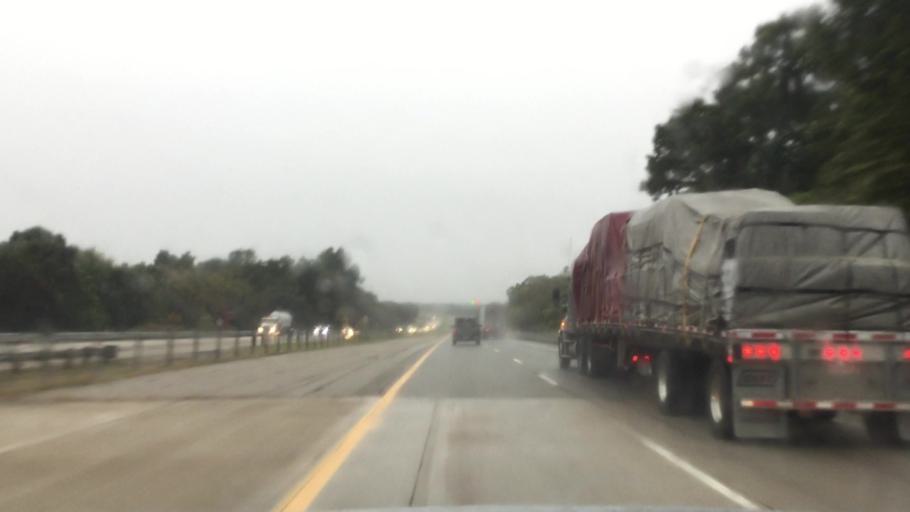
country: US
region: Michigan
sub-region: Van Buren County
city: Mattawan
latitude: 42.2232
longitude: -85.7675
